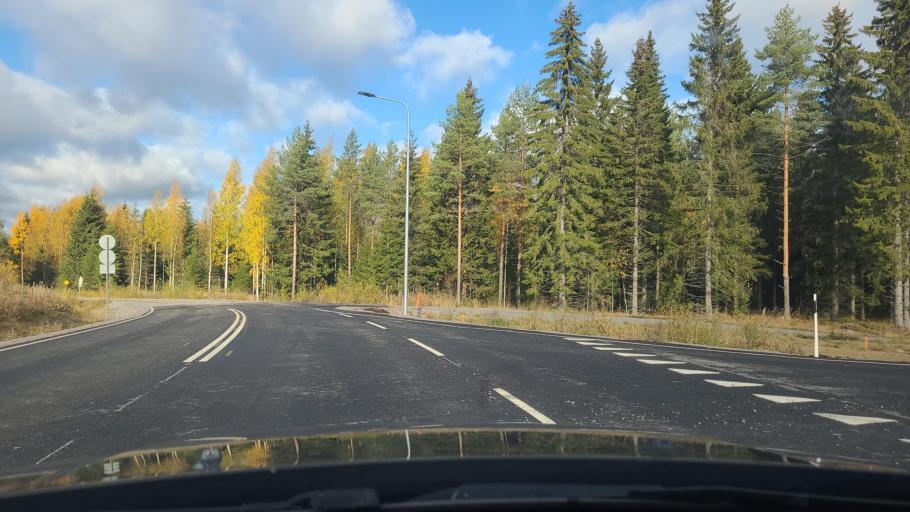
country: FI
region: Southern Savonia
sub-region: Pieksaemaeki
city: Juva
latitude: 61.8595
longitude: 27.7144
